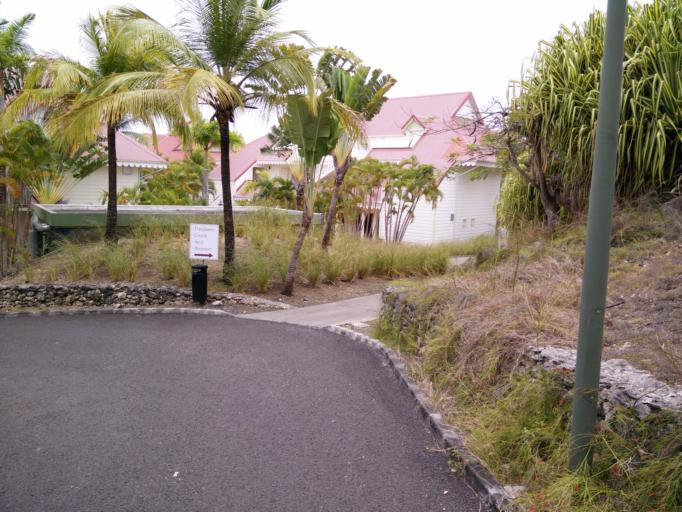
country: GP
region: Guadeloupe
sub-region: Guadeloupe
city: Sainte-Anne
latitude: 16.2428
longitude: -61.3302
